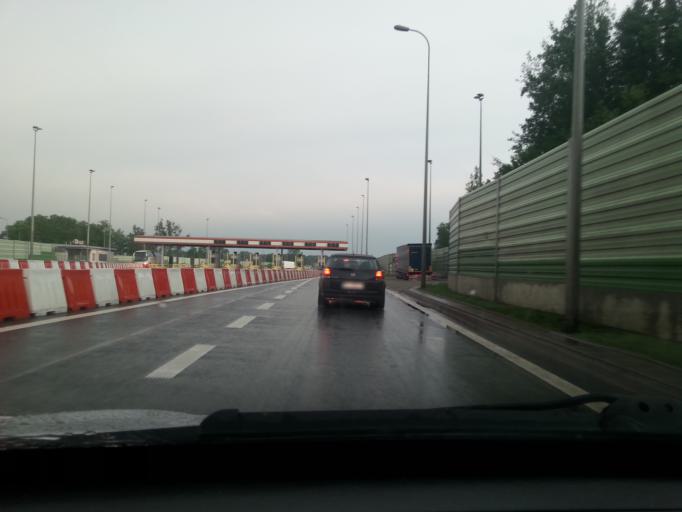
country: PL
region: Lodz Voivodeship
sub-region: Powiat zgierski
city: Strykow
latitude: 51.8861
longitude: 19.5848
